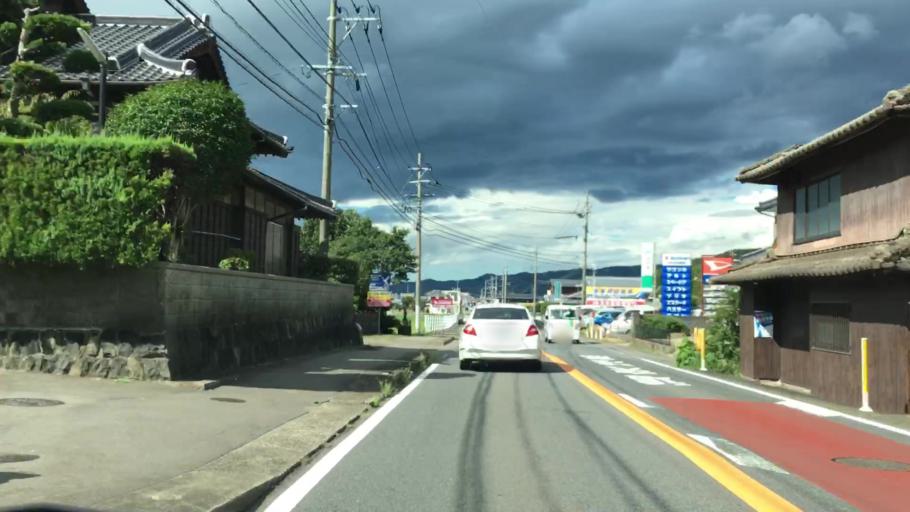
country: JP
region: Saga Prefecture
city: Imaricho-ko
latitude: 33.2460
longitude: 129.8515
